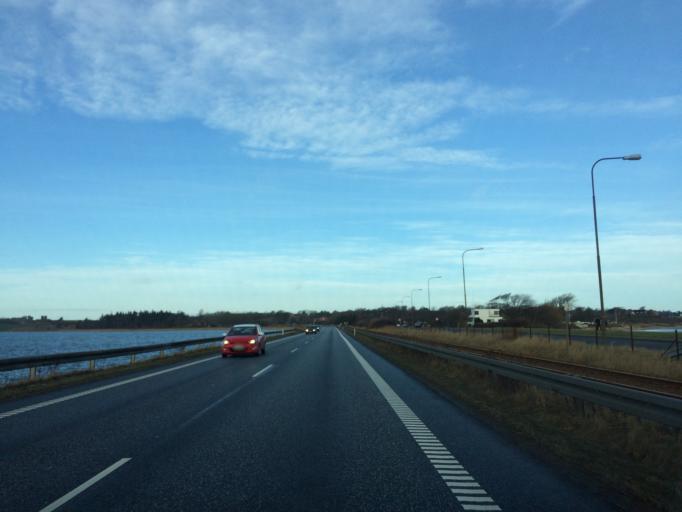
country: DK
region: Central Jutland
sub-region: Struer Kommune
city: Struer
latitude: 56.4983
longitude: 8.5825
